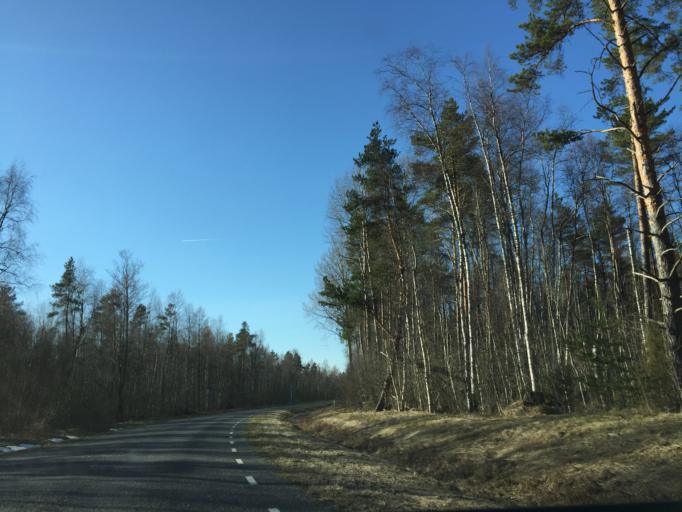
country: RU
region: Pskov
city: Gdov
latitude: 59.0005
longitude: 27.6968
